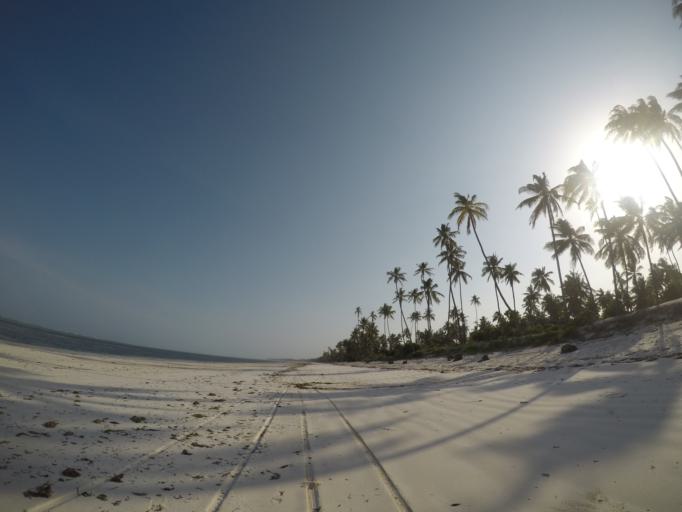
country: TZ
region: Zanzibar Central/South
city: Nganane
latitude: -6.2064
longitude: 39.5348
